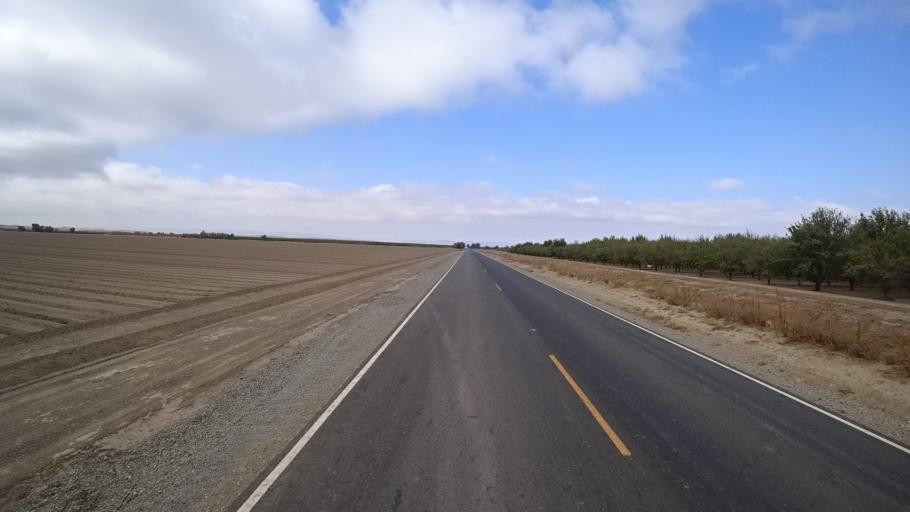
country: US
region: California
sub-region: Yolo County
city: Woodland
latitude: 38.7940
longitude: -121.8514
